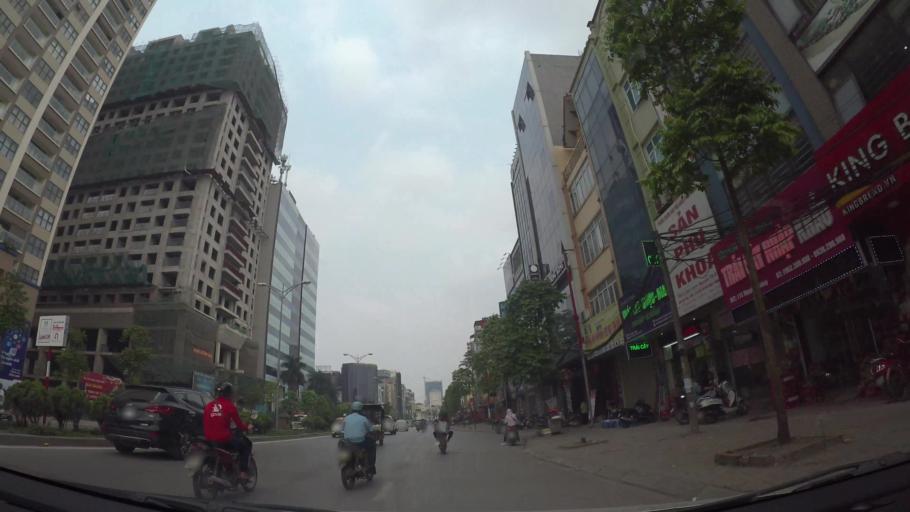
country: VN
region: Ha Noi
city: Cau Dien
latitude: 21.0332
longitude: 105.7705
